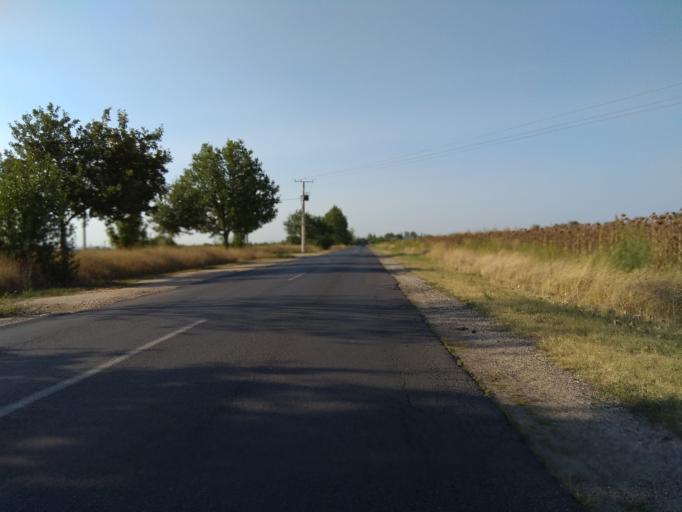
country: HU
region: Borsod-Abauj-Zemplen
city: Onod
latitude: 47.9893
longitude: 20.9237
